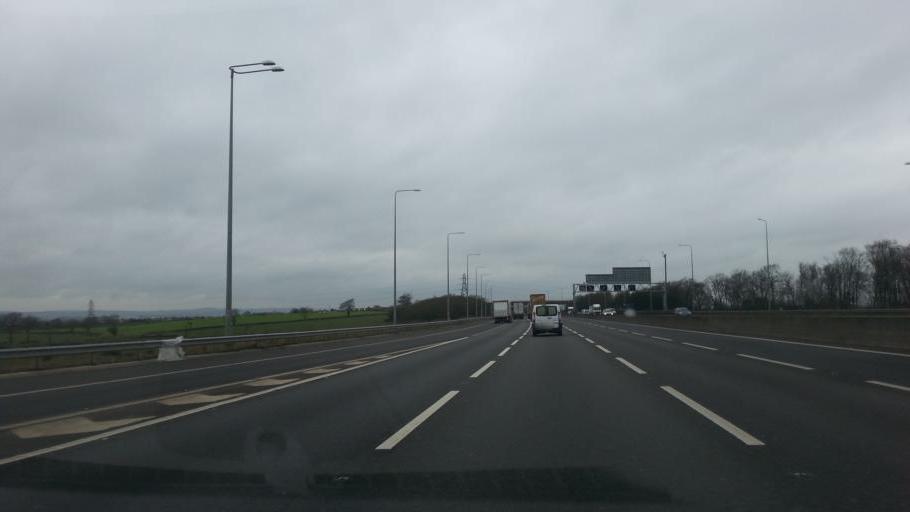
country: GB
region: England
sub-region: Nottinghamshire
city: Kirkby in Ashfield
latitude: 53.0661
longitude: -1.2723
